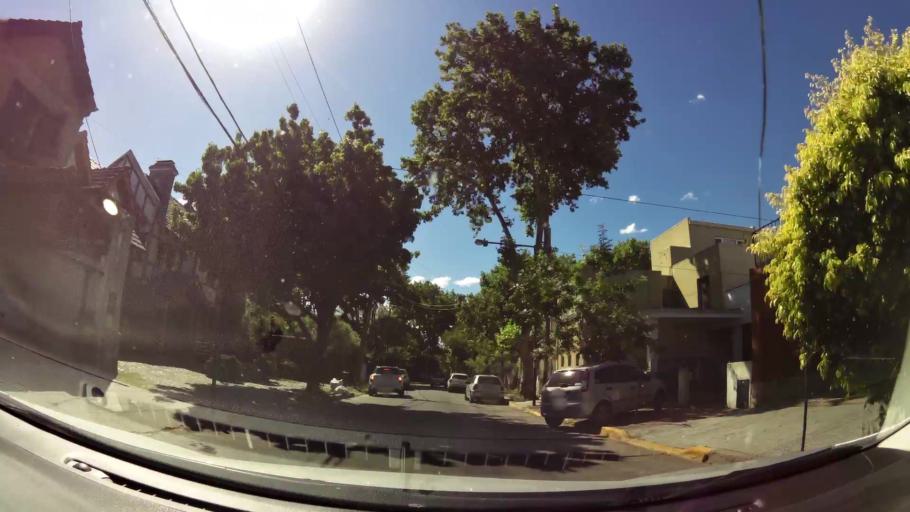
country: AR
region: Buenos Aires
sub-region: Partido de San Isidro
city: San Isidro
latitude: -34.4638
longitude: -58.5178
